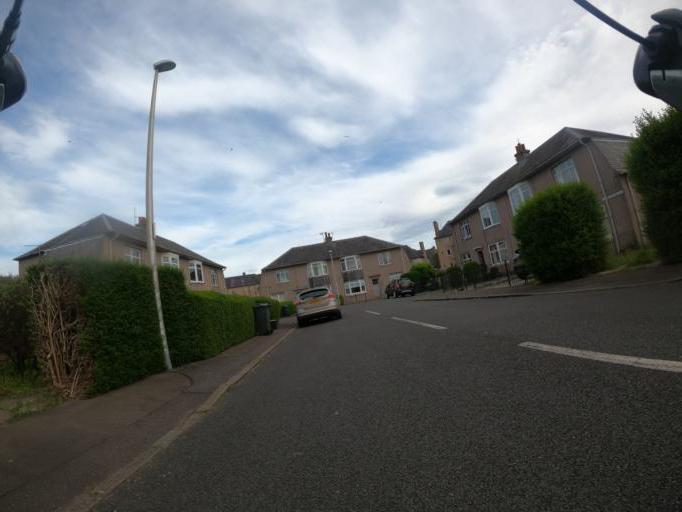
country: GB
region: Scotland
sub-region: Edinburgh
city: Edinburgh
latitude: 55.9770
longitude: -3.2222
